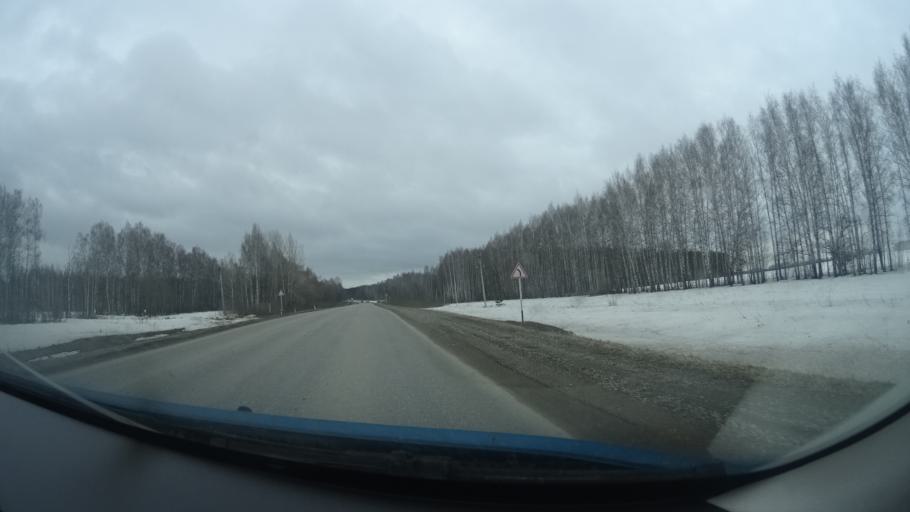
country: RU
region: Bashkortostan
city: Birsk
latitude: 55.3402
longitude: 55.5932
